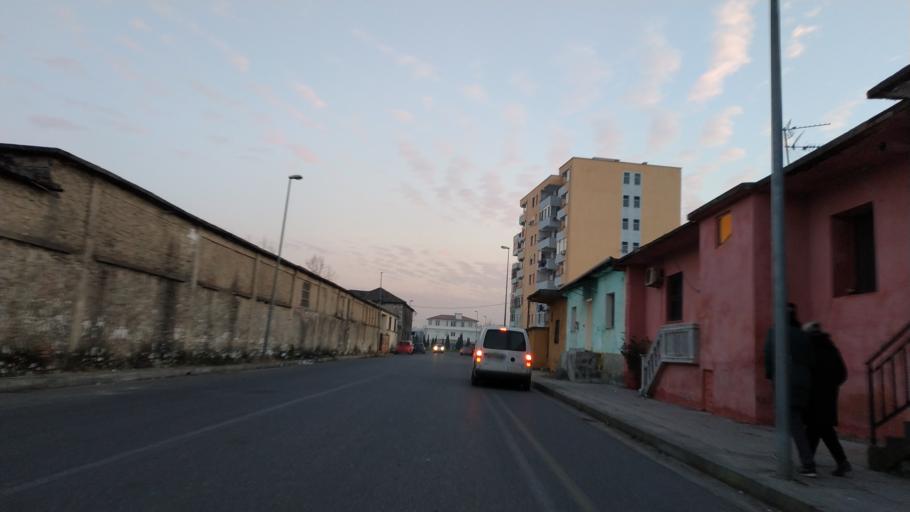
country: AL
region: Shkoder
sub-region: Rrethi i Shkodres
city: Shkoder
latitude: 42.0767
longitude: 19.5238
